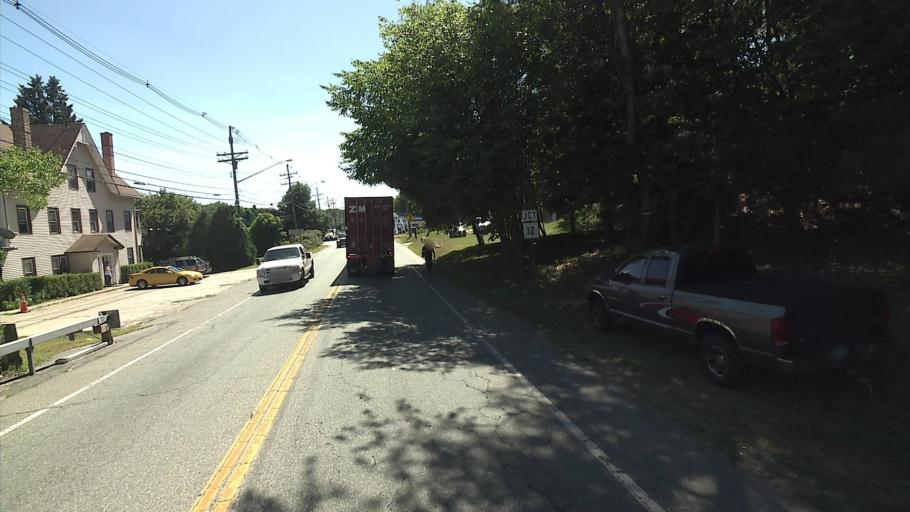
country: US
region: Connecticut
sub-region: New London County
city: Norwich
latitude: 41.5584
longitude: -72.0487
